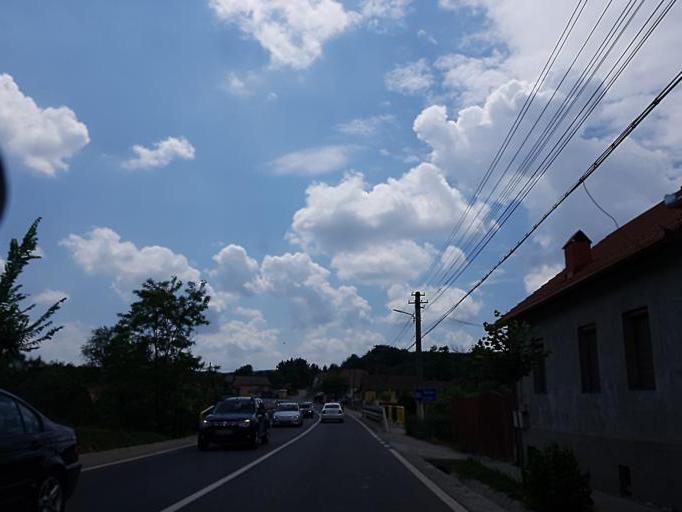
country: RO
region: Sibiu
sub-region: Comuna Slimnic
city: Slimnic
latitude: 45.9155
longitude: 24.1539
